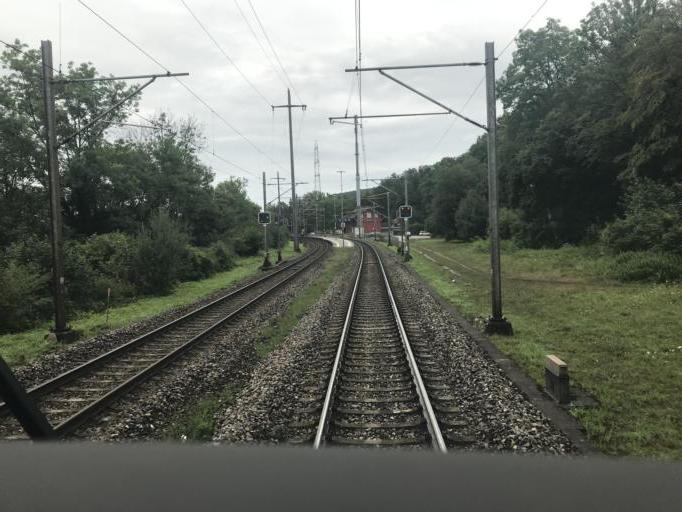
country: CH
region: Zurich
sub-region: Bezirk Buelach
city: Glattfelden
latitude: 47.5468
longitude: 8.5231
